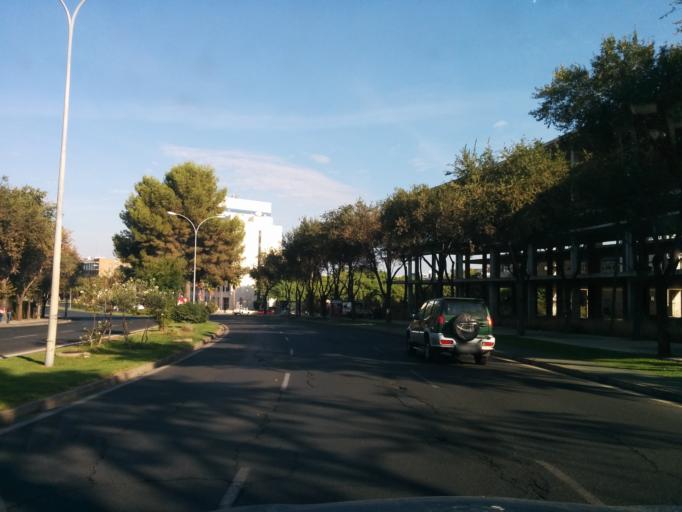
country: ES
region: Andalusia
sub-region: Provincia de Sevilla
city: Sevilla
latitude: 37.4042
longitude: -5.9285
